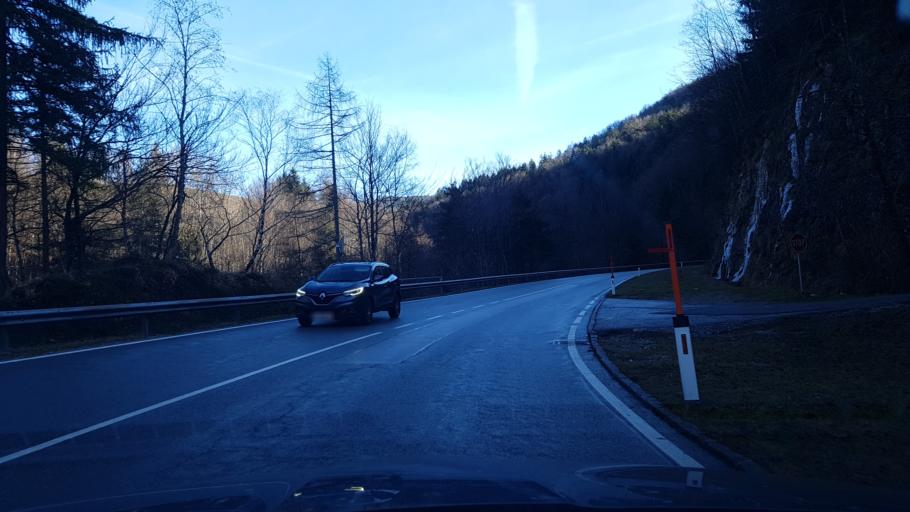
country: AT
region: Salzburg
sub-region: Politischer Bezirk Hallein
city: Krispl
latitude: 47.7312
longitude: 13.1465
